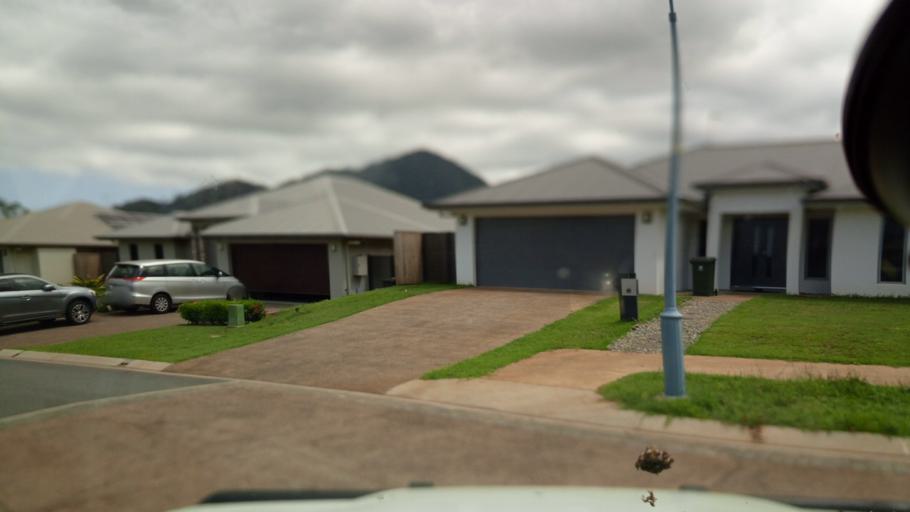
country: AU
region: Queensland
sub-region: Cairns
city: Redlynch
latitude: -16.8970
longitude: 145.6935
